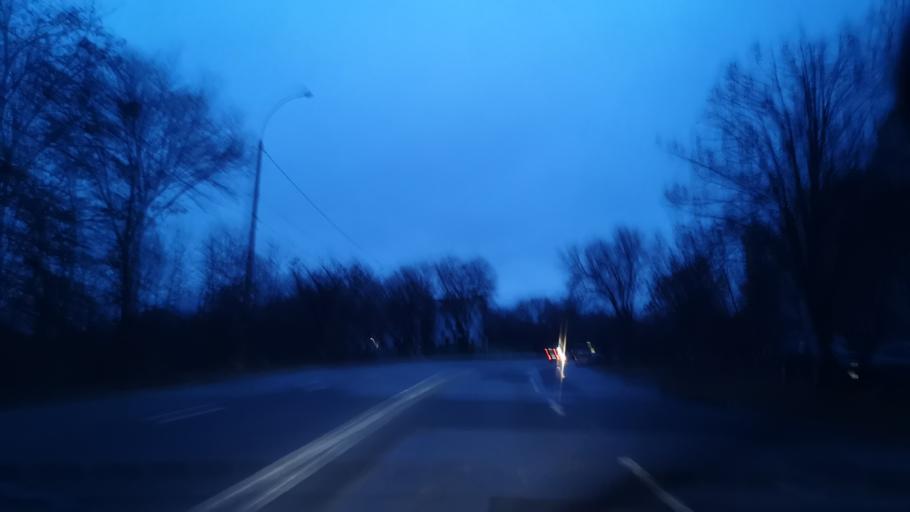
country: MD
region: Chisinau
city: Chisinau
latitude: 47.0335
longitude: 28.8782
